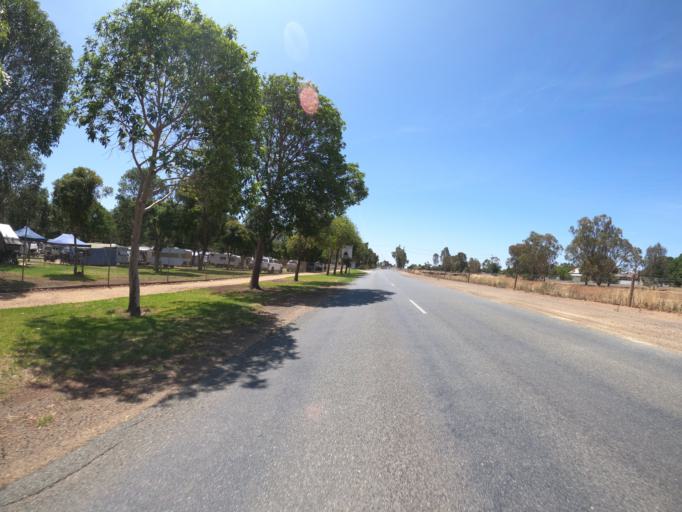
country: AU
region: Victoria
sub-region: Moira
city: Yarrawonga
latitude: -36.0122
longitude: 145.9982
